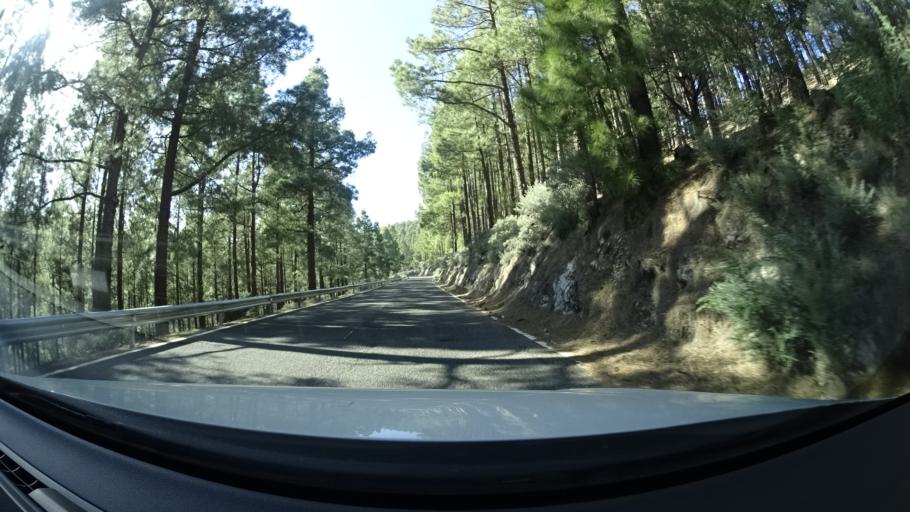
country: ES
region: Canary Islands
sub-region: Provincia de Las Palmas
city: Vega de San Mateo
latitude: 27.9656
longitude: -15.5430
